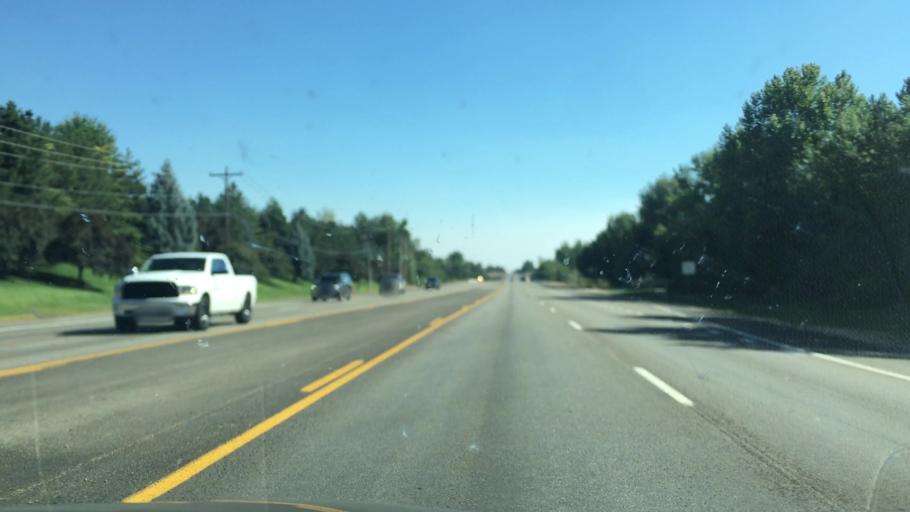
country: US
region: Idaho
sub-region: Ada County
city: Eagle
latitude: 43.6789
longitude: -116.3542
